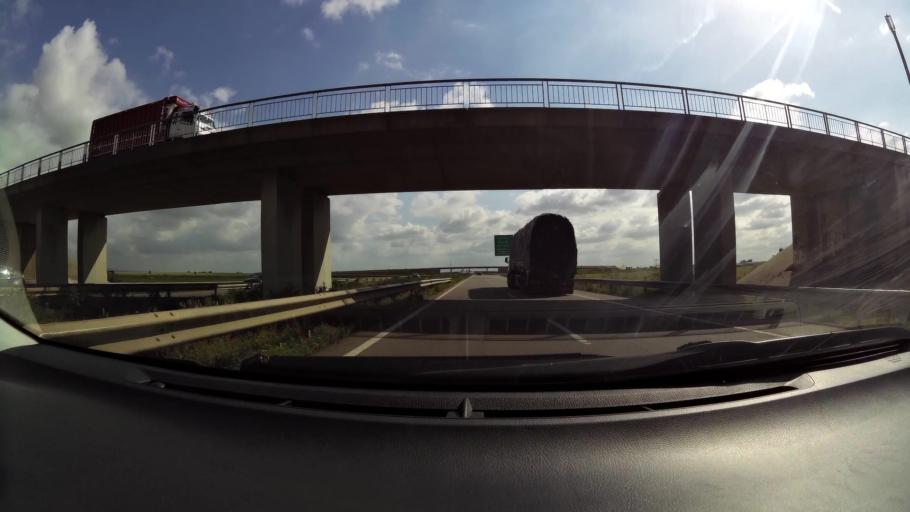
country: MA
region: Chaouia-Ouardigha
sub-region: Settat Province
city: Berrechid
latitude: 33.2494
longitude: -7.5631
